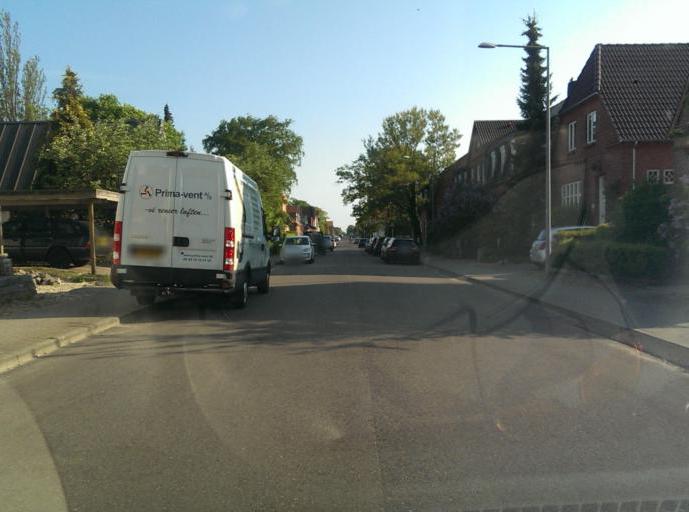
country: DK
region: South Denmark
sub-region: Esbjerg Kommune
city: Esbjerg
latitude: 55.4778
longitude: 8.4529
